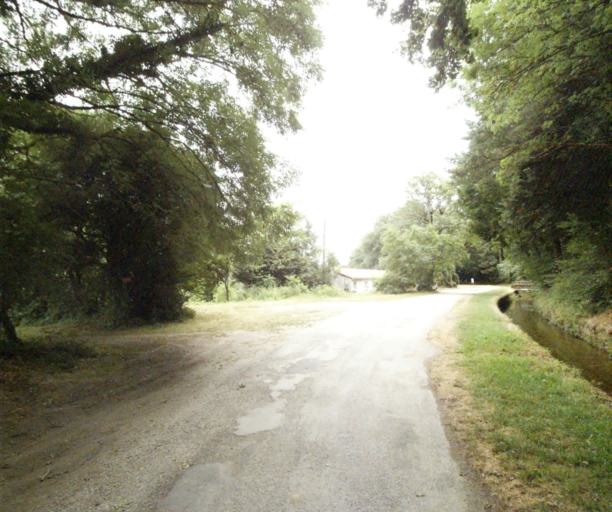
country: FR
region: Midi-Pyrenees
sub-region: Departement du Tarn
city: Soreze
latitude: 43.4092
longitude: 2.0878
